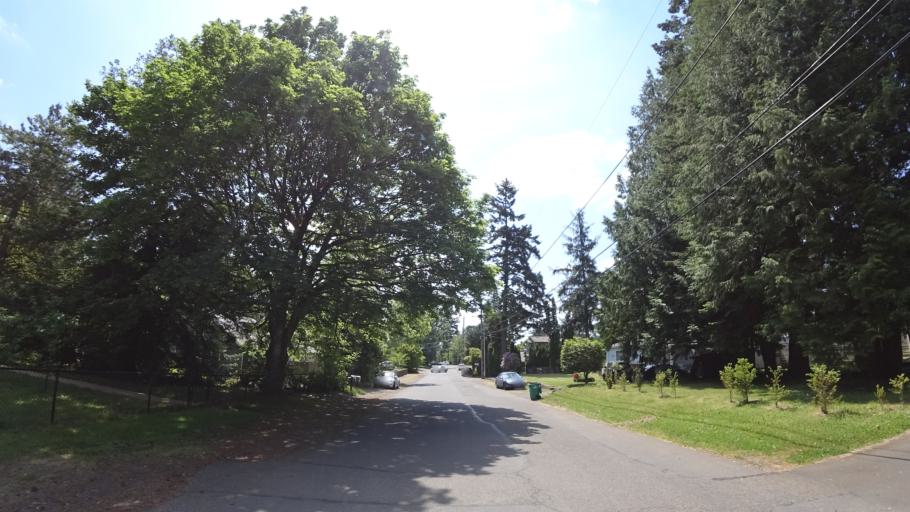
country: US
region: Oregon
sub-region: Multnomah County
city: Fairview
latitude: 45.5278
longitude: -122.5015
